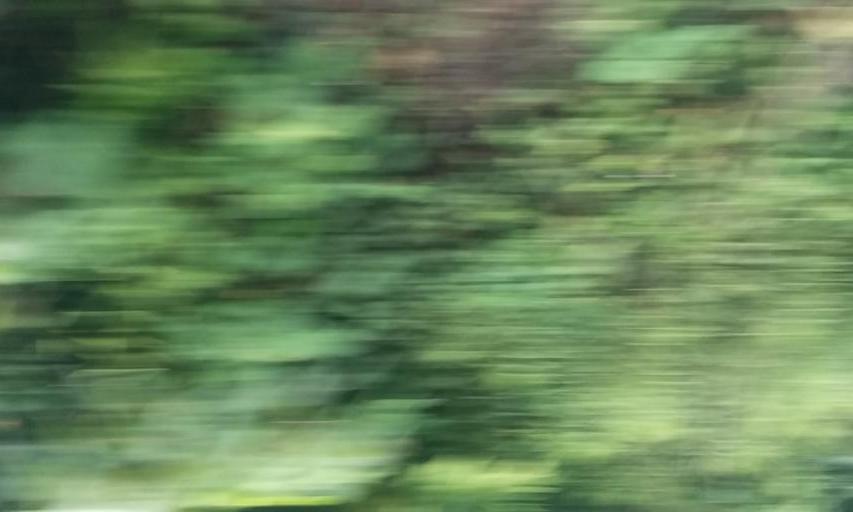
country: JP
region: Chiba
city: Nagareyama
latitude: 35.8424
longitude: 139.9095
